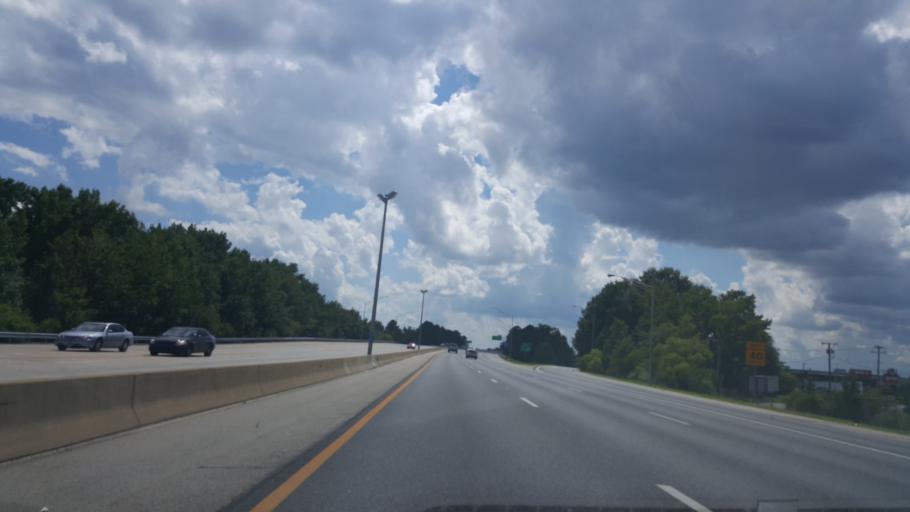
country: US
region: Virginia
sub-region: City of Newport News
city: Newport News
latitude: 37.0072
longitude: -76.4000
